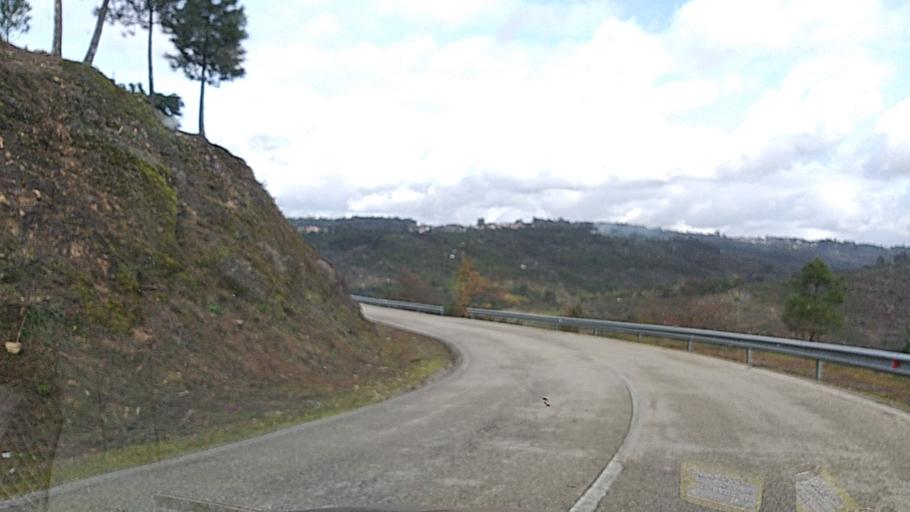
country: PT
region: Viseu
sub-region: Satao
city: Satao
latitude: 40.6628
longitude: -7.6674
